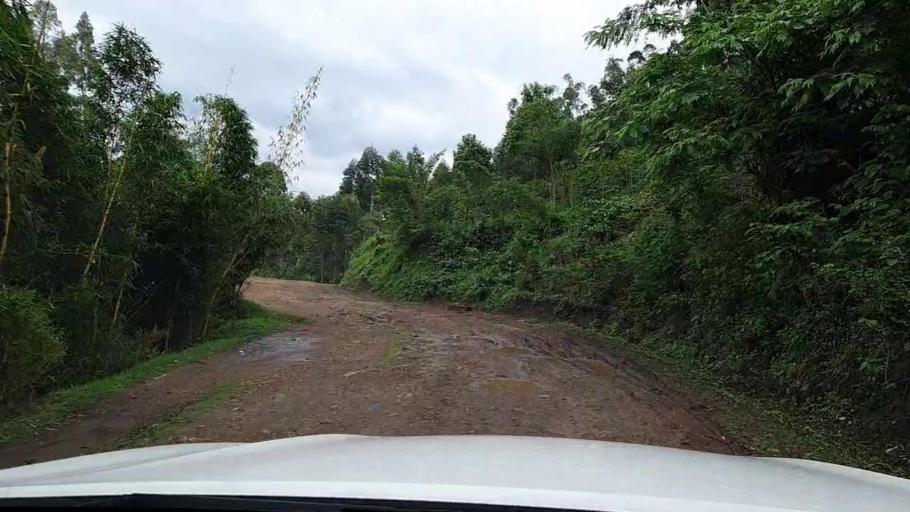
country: RW
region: Western Province
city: Cyangugu
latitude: -2.5541
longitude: 29.0360
